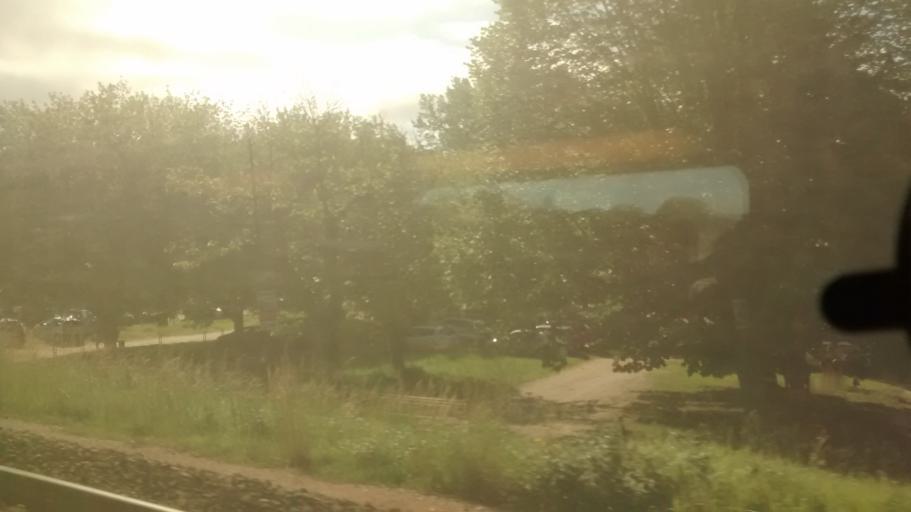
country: FR
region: Pays de la Loire
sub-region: Departement de la Sarthe
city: Sarge-les-le-Mans
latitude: 48.0020
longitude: 0.2493
